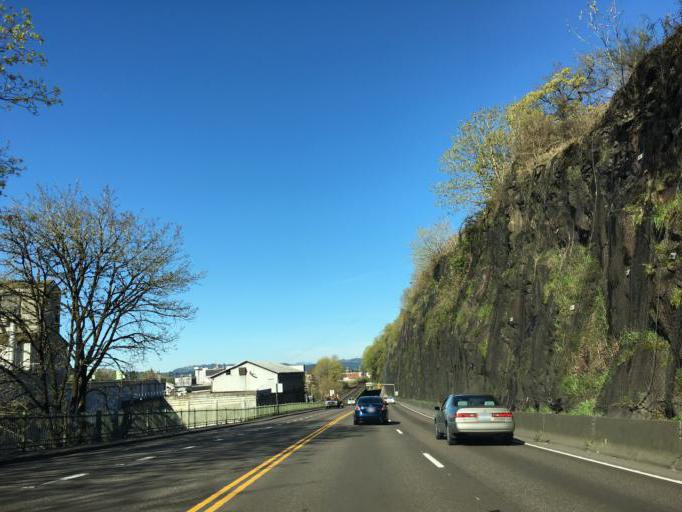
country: US
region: Oregon
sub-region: Clackamas County
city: Oregon City
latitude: 45.3532
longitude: -122.6125
